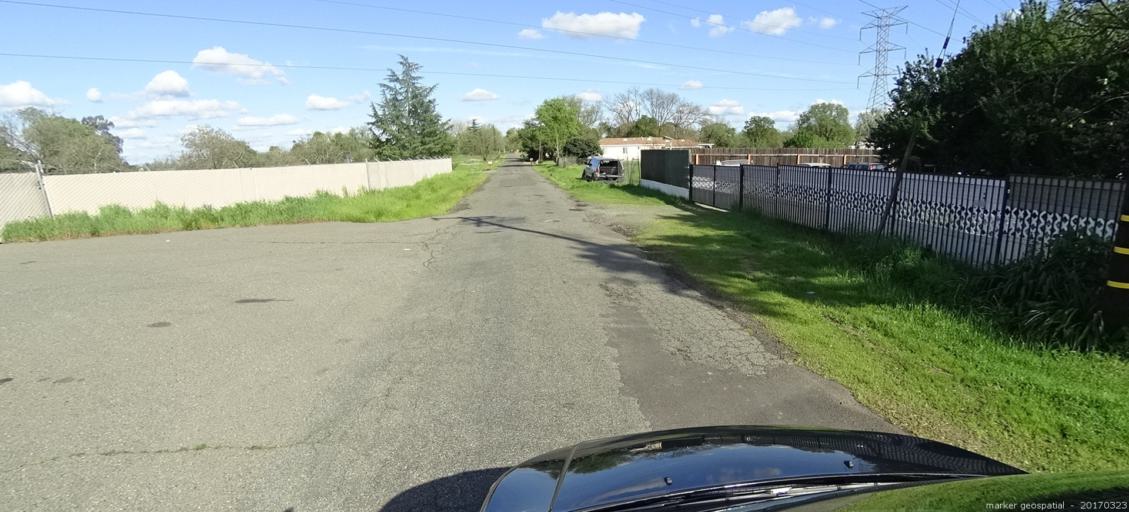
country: US
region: California
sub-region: Sacramento County
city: Rosemont
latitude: 38.5221
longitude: -121.3670
